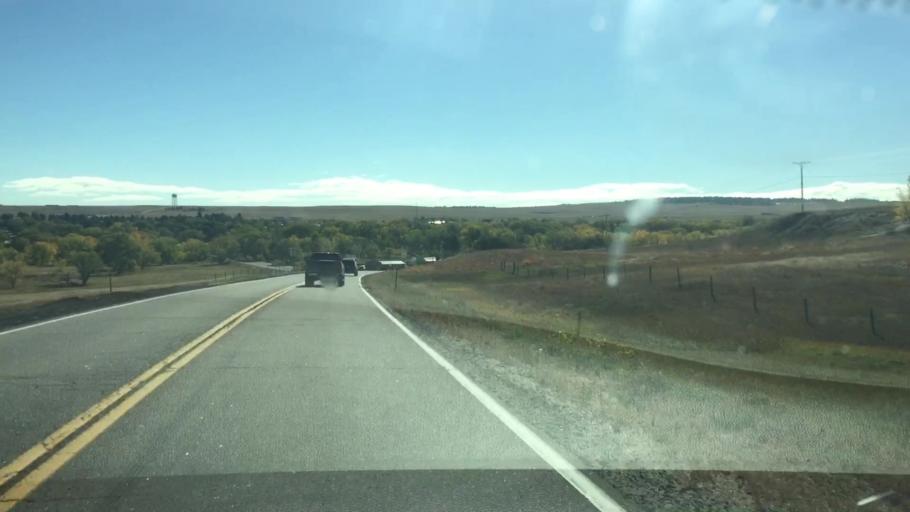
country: US
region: Colorado
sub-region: Elbert County
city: Kiowa
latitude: 39.3480
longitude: -104.4776
